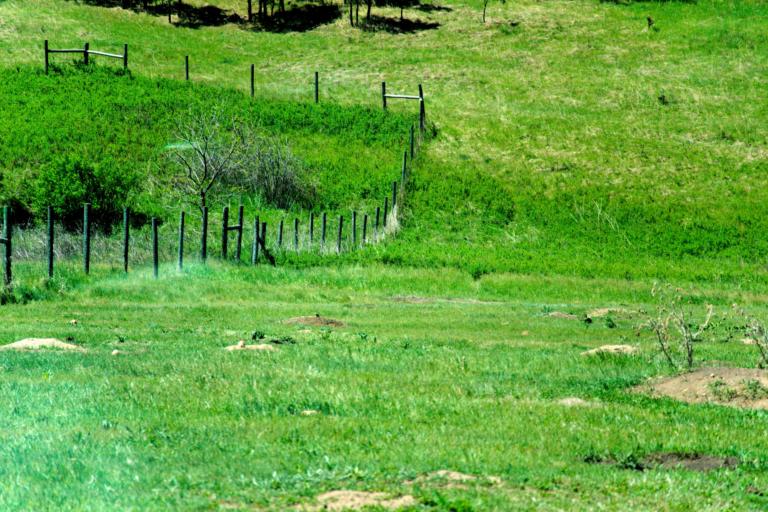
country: US
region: South Dakota
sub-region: Custer County
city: Custer
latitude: 43.6836
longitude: -103.4498
